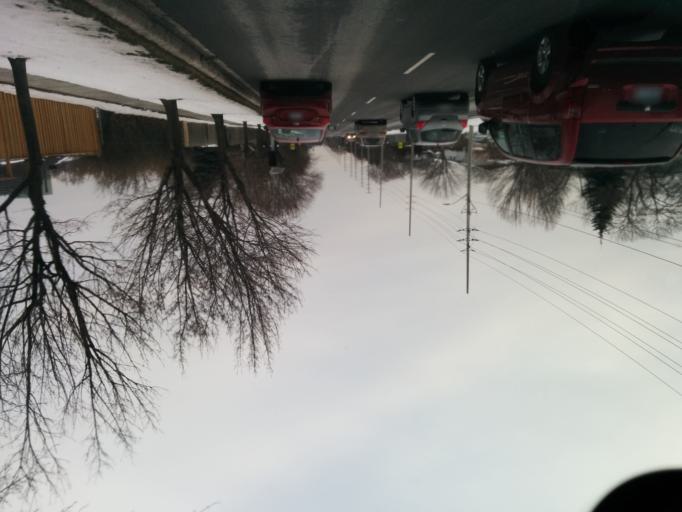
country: CA
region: Ontario
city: Etobicoke
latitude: 43.6056
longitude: -79.6006
